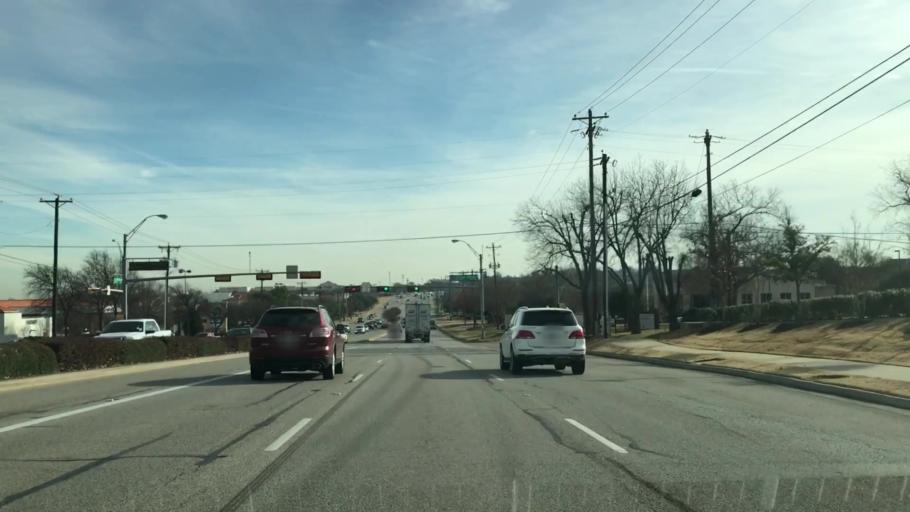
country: US
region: Texas
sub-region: Tarrant County
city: Southlake
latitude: 32.9409
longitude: -97.1237
